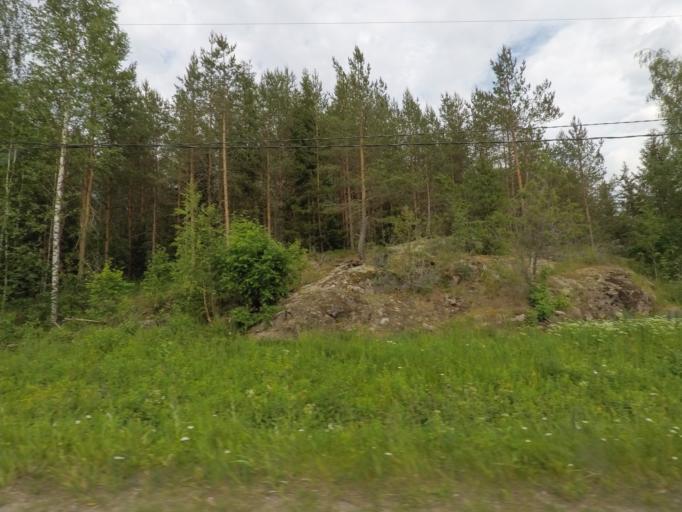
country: FI
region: Paijanne Tavastia
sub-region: Lahti
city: Hollola
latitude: 60.8793
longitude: 25.5052
